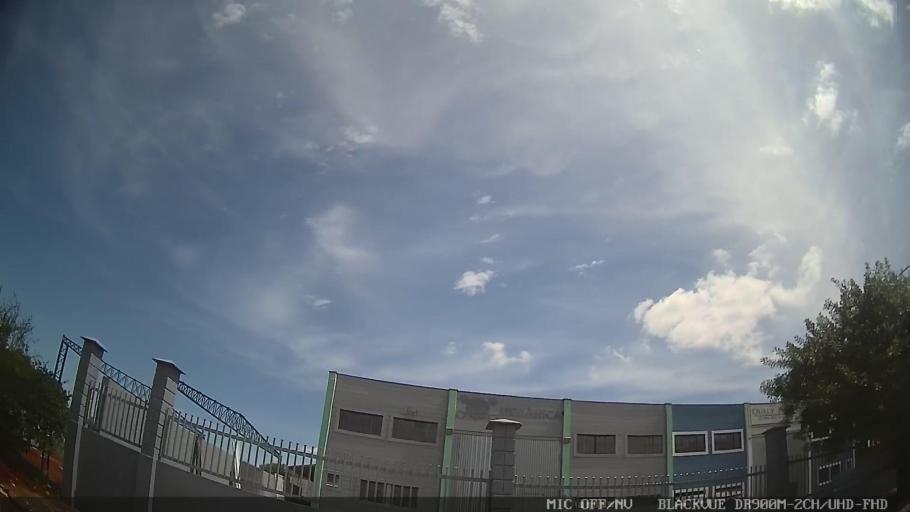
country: BR
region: Sao Paulo
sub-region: Artur Nogueira
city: Artur Nogueira
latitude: -22.6144
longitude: -47.0615
